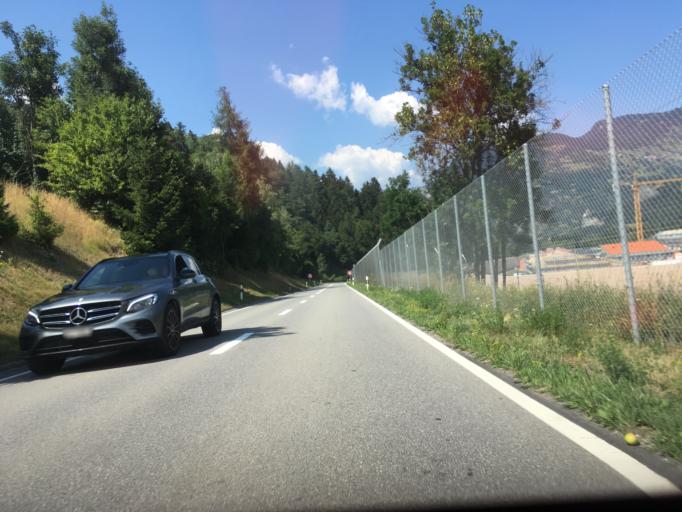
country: CH
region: Grisons
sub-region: Hinterrhein District
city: Cazis
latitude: 46.7341
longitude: 9.4252
